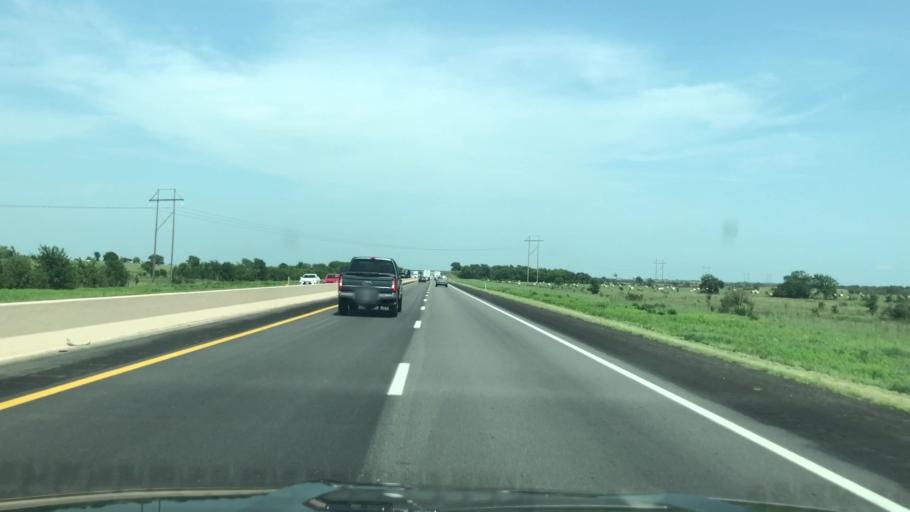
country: US
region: Oklahoma
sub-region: Craig County
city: Vinita
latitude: 36.6730
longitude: -95.0616
